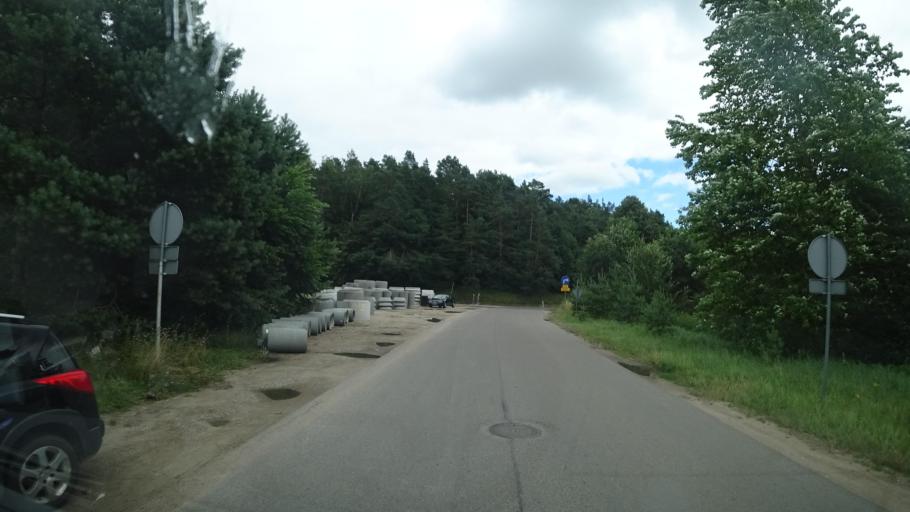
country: PL
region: Warmian-Masurian Voivodeship
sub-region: Powiat goldapski
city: Goldap
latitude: 54.3332
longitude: 22.2940
